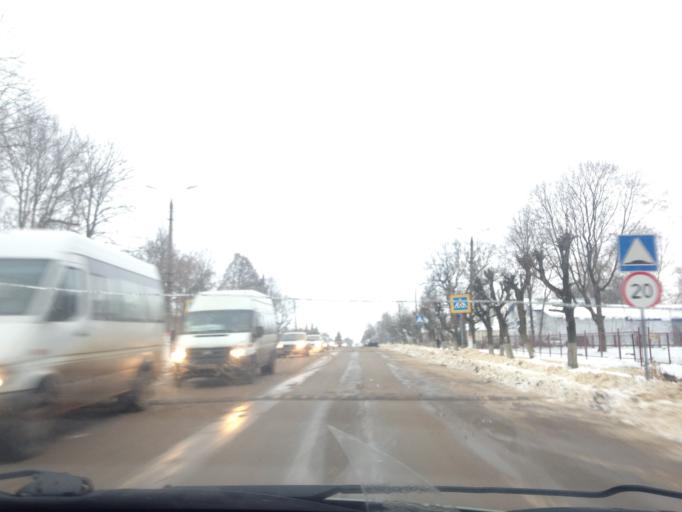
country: RU
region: Tula
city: Shchekino
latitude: 54.0009
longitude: 37.5103
